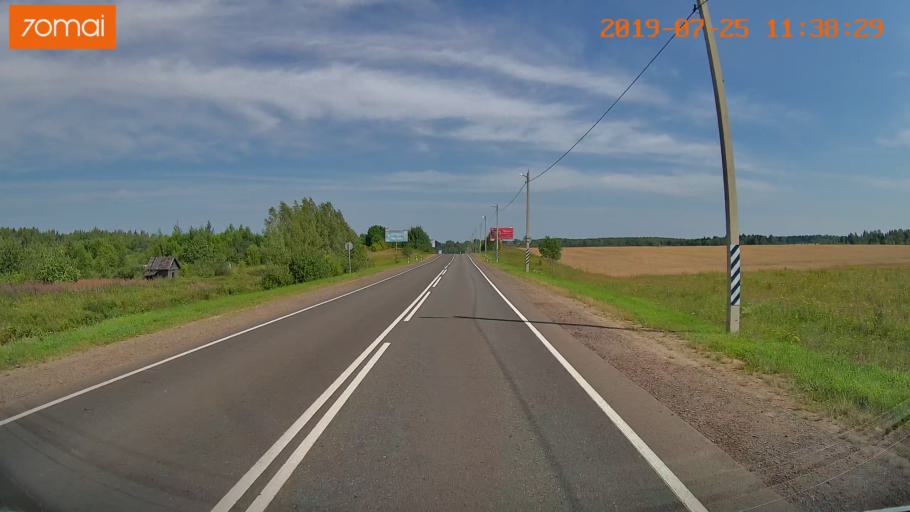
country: RU
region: Ivanovo
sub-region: Privolzhskiy Rayon
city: Ples
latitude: 57.4417
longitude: 41.4837
